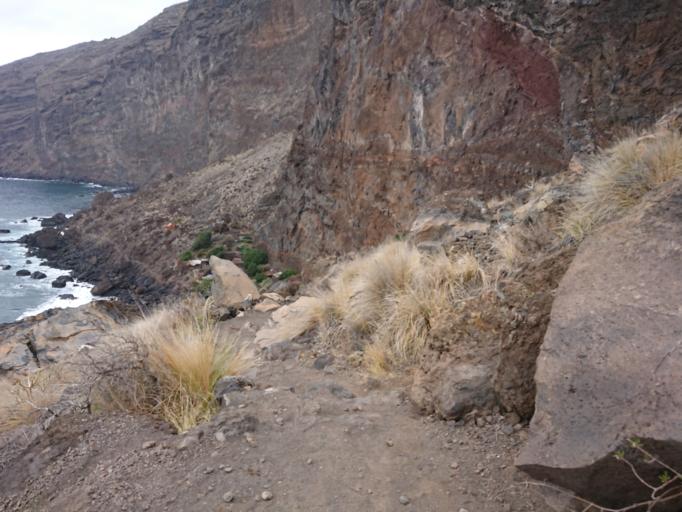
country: ES
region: Canary Islands
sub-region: Provincia de Santa Cruz de Tenerife
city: Tijarafe
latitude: 28.7203
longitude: -17.9791
